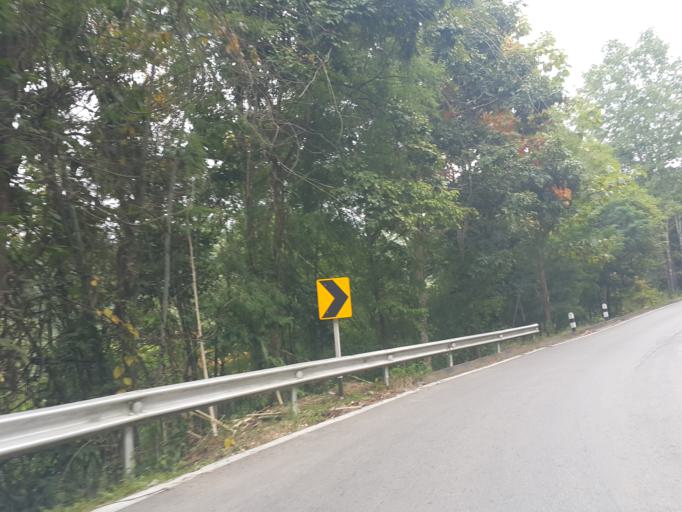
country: TH
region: Mae Hong Son
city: Mae Hi
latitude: 19.2714
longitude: 98.5011
